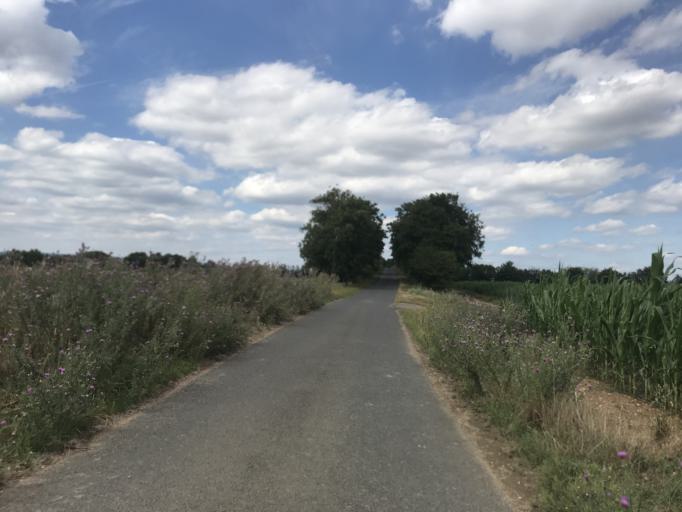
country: DE
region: Hesse
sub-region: Regierungsbezirk Darmstadt
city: Hochheim am Main
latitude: 50.0238
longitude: 8.3132
